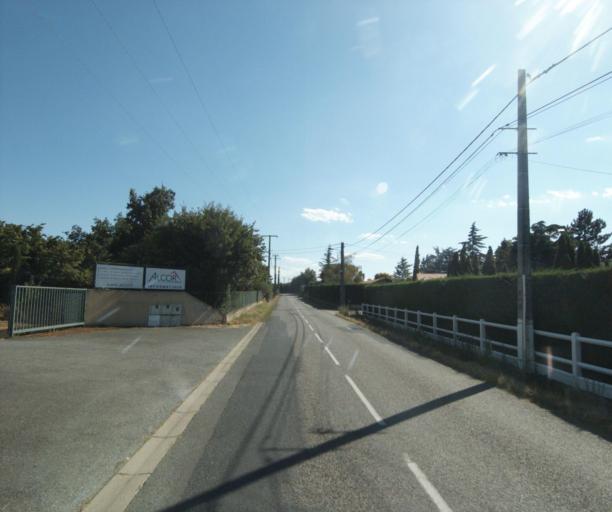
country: FR
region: Rhone-Alpes
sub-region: Departement du Rhone
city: La Tour-de-Salvagny
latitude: 45.8391
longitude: 4.7215
